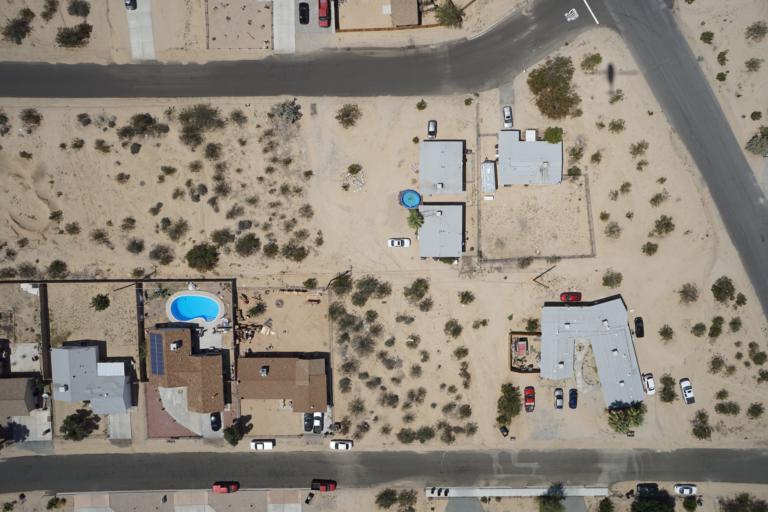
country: US
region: California
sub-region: San Bernardino County
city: Twentynine Palms
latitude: 34.1392
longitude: -116.0579
